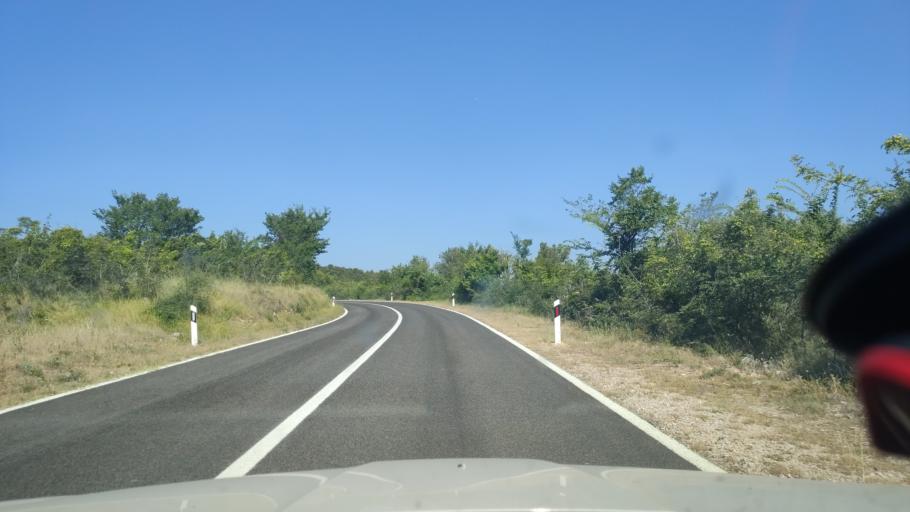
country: HR
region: Sibensko-Kniniska
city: Zaton
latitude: 43.9156
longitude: 15.8319
